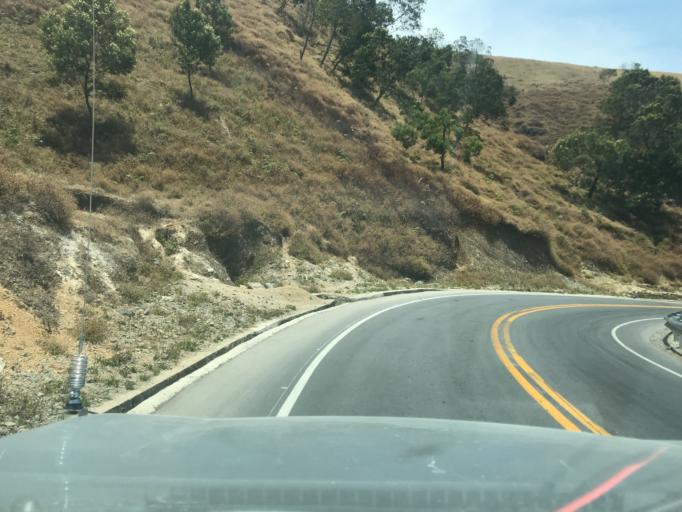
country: TL
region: Manufahi
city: Same
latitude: -8.8824
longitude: 125.6054
